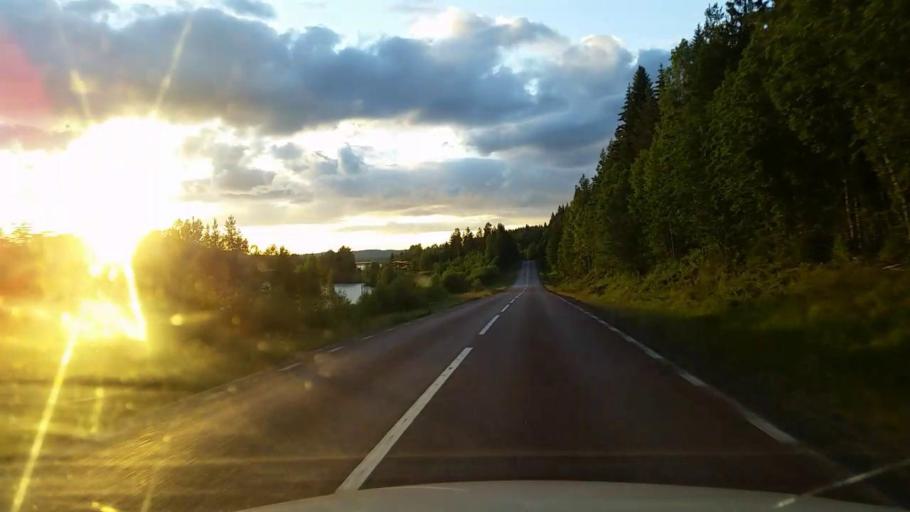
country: SE
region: Vaesternorrland
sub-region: Ange Kommun
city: Ange
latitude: 62.1468
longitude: 15.6846
